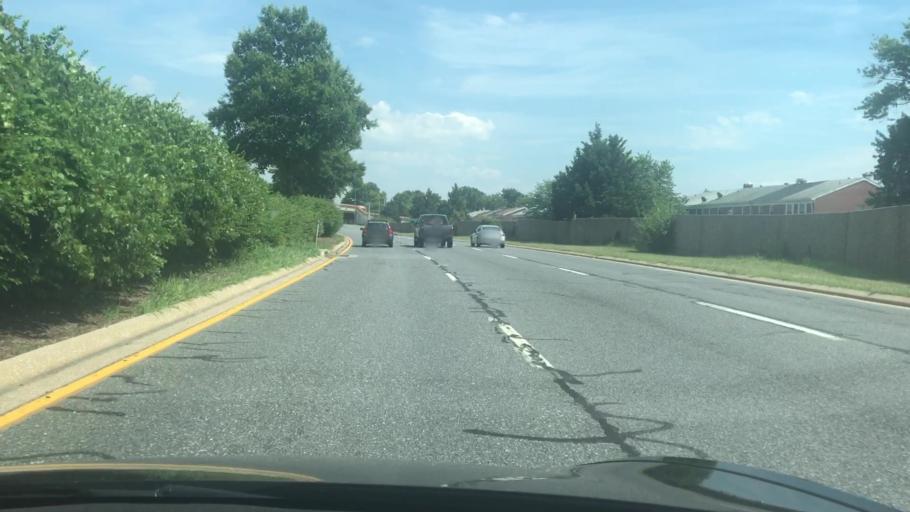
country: US
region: Maryland
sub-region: Baltimore County
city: Essex
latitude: 39.3075
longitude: -76.4501
